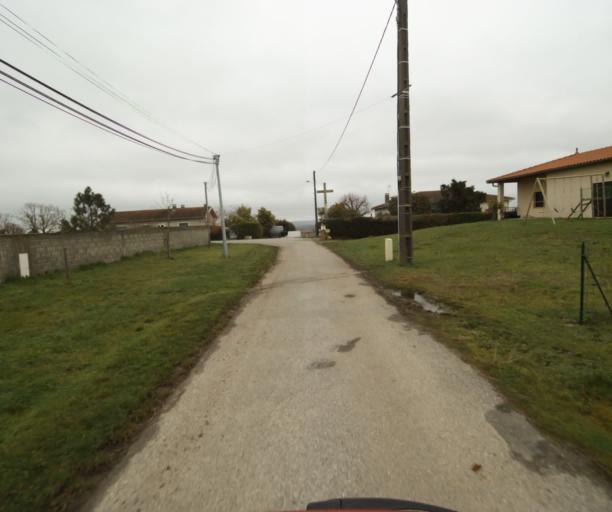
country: FR
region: Midi-Pyrenees
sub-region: Departement de la Haute-Garonne
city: Gaillac-Toulza
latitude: 43.2604
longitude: 1.5172
